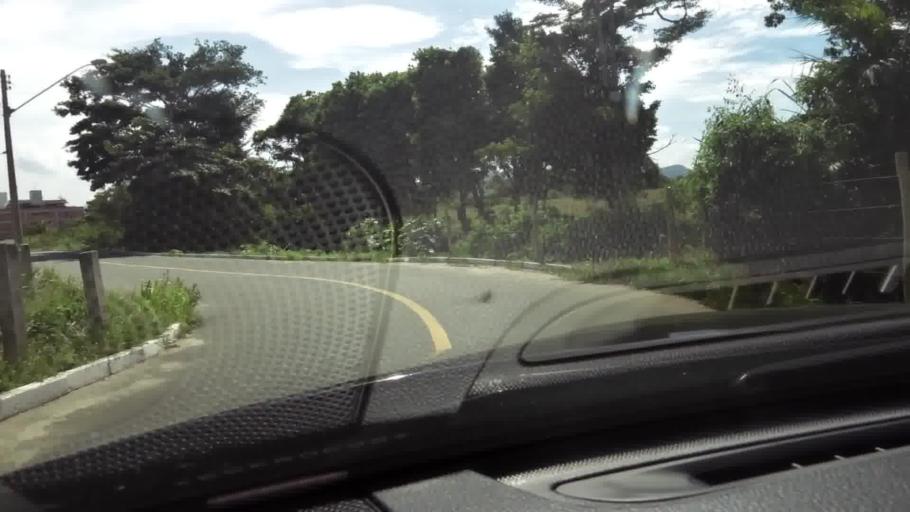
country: BR
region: Espirito Santo
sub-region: Guarapari
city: Guarapari
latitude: -20.6500
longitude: -40.4755
